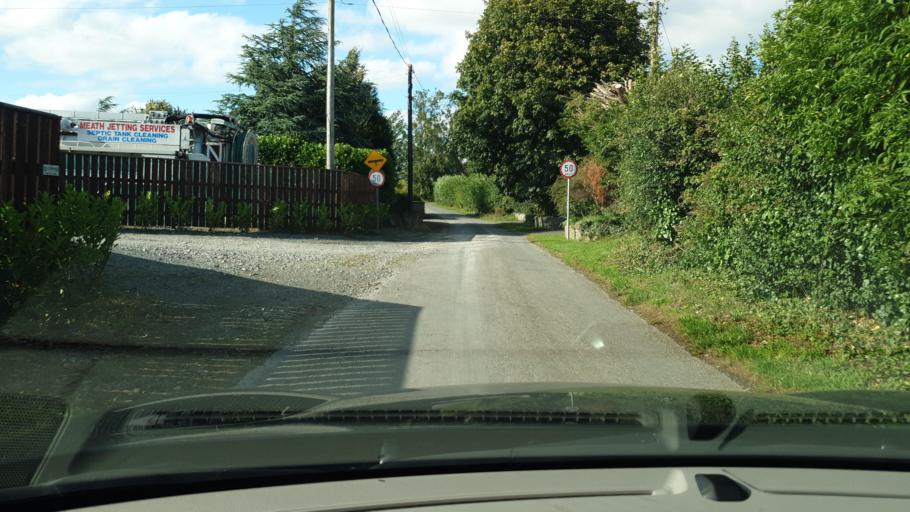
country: IE
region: Leinster
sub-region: An Mhi
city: Ashbourne
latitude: 53.5870
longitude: -6.3493
